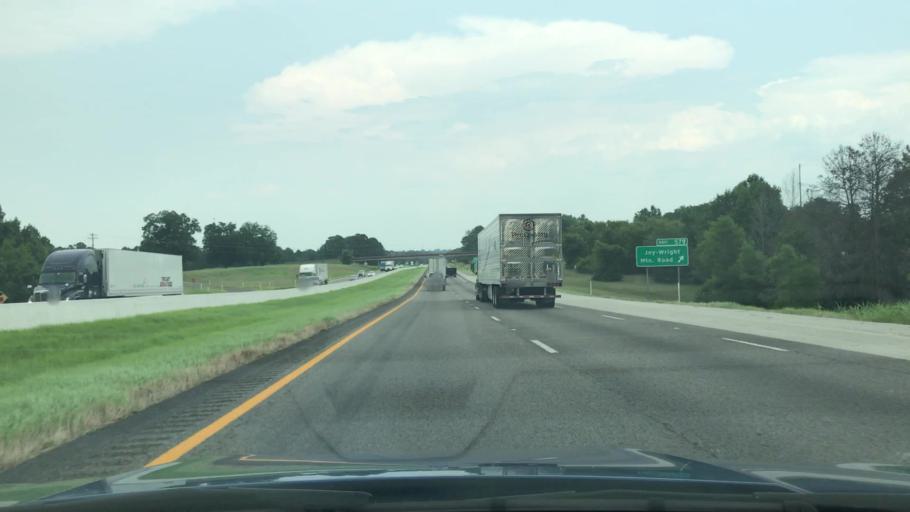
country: US
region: Texas
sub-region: Gregg County
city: Liberty City
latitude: 32.4364
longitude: -94.9944
